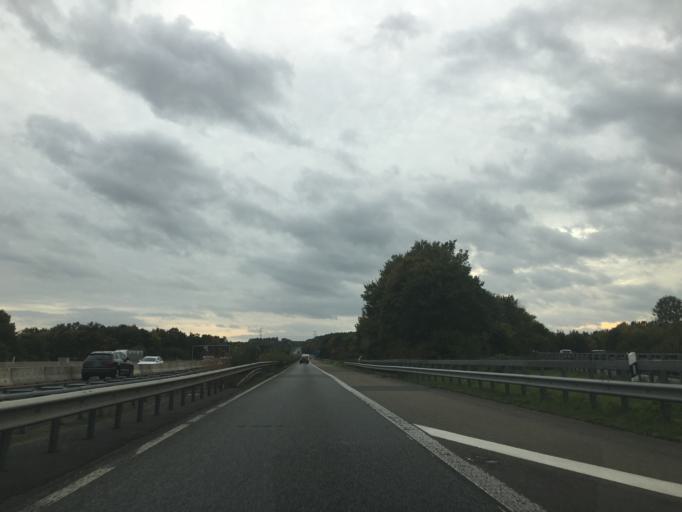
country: DE
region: Rheinland-Pfalz
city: Bassenheim
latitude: 50.3612
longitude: 7.4873
